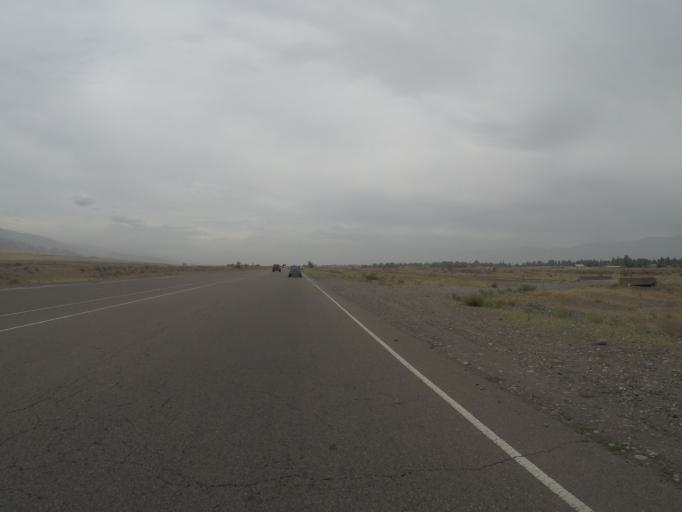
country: KG
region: Chuy
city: Bystrovka
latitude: 42.8302
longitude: 75.5150
